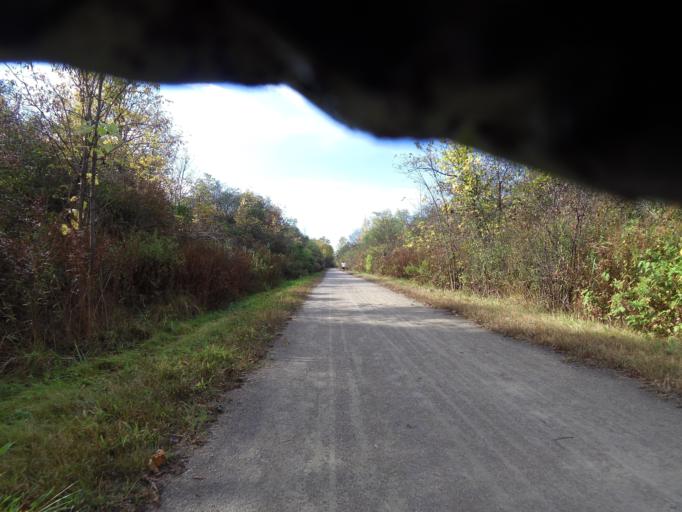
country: CA
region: Ontario
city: Brantford
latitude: 43.1504
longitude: -80.1903
